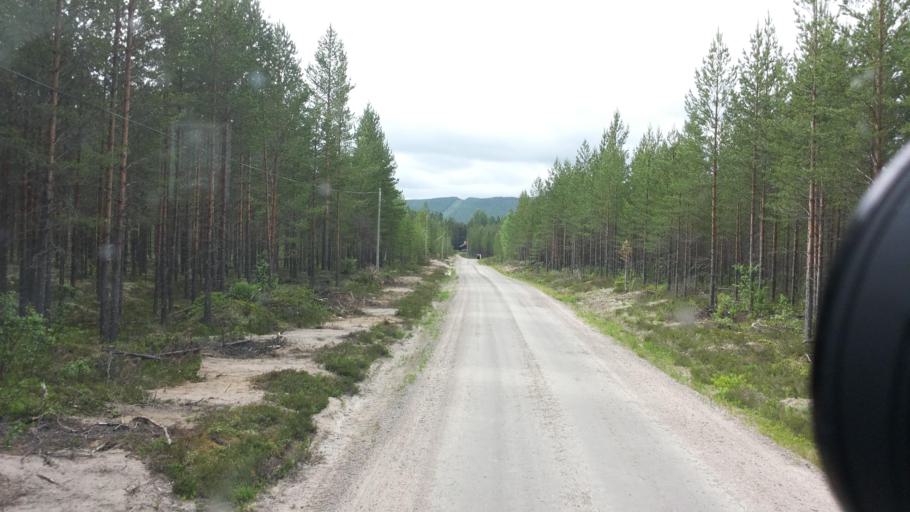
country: SE
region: Gaevleborg
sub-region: Ovanakers Kommun
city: Edsbyn
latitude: 61.5178
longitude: 15.3541
